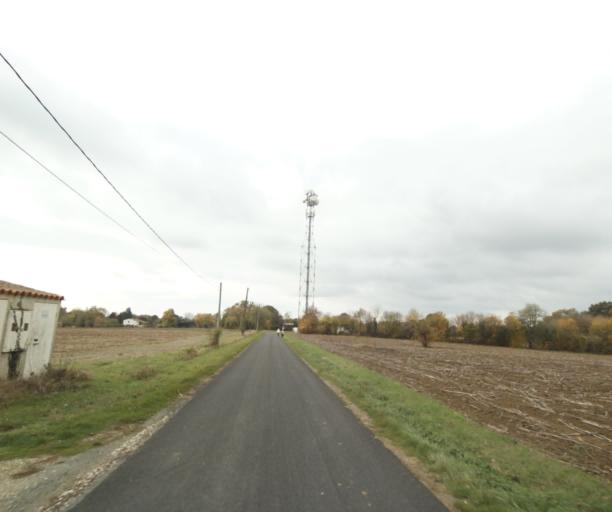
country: FR
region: Poitou-Charentes
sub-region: Departement de la Charente-Maritime
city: Saint-Georges-des-Coteaux
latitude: 45.7794
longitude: -0.6896
